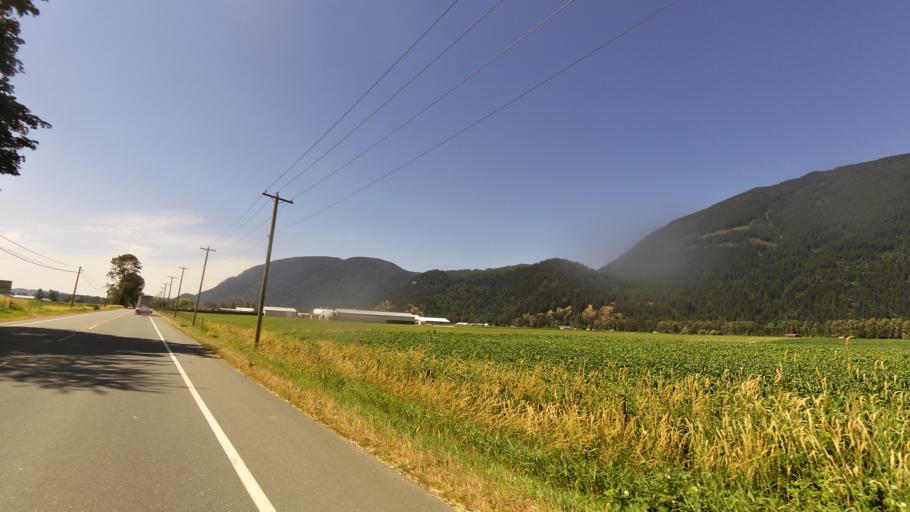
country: CA
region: British Columbia
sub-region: Fraser Valley Regional District
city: Chilliwack
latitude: 49.1693
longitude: -122.1052
